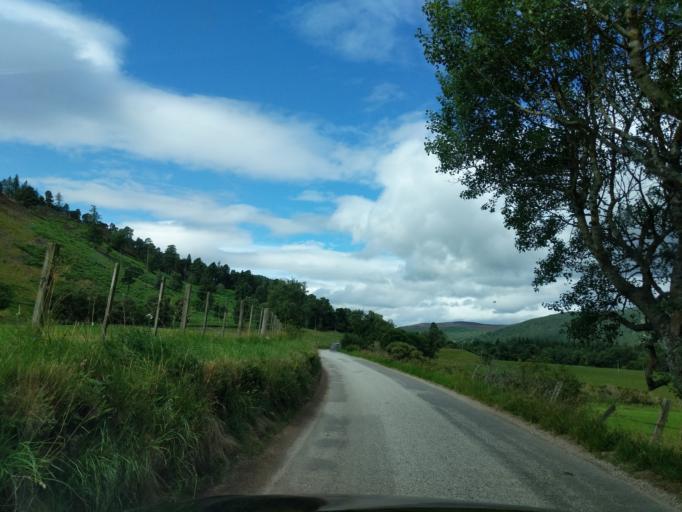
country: GB
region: Scotland
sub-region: Aberdeenshire
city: Ballater
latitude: 57.0471
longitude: -3.1025
